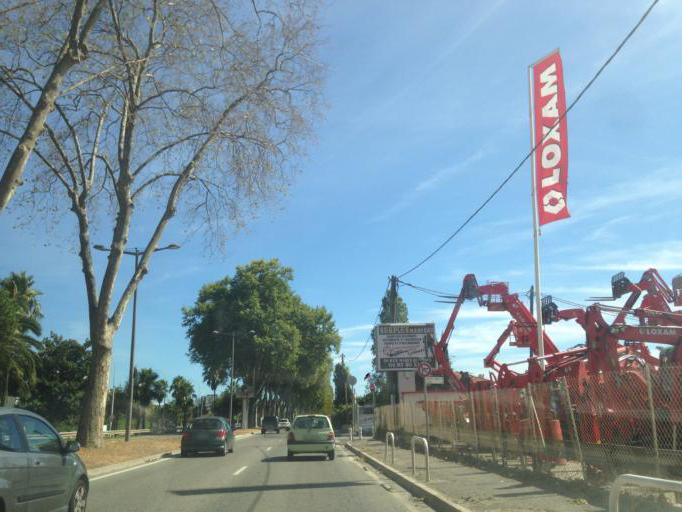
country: FR
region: Provence-Alpes-Cote d'Azur
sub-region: Departement des Alpes-Maritimes
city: Saint-Laurent-du-Var
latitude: 43.6866
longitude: 7.1973
